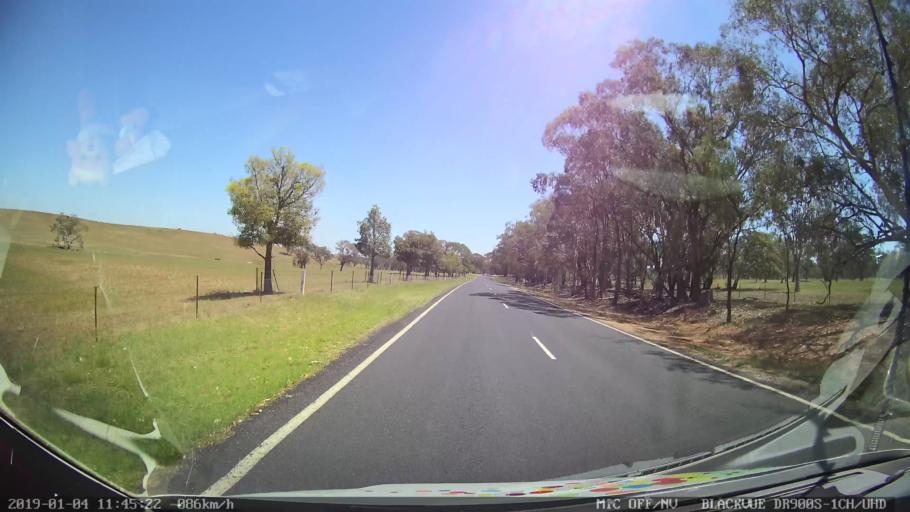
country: AU
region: New South Wales
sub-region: Cabonne
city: Molong
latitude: -32.9545
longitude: 148.7637
